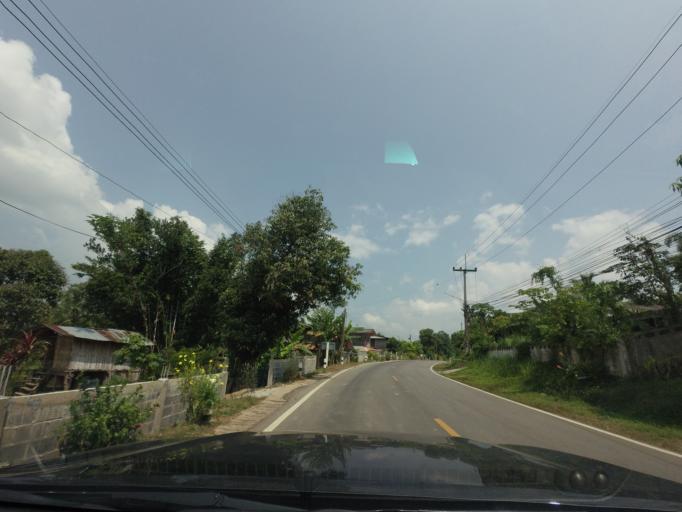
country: TH
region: Nan
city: Santi Suk
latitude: 18.9573
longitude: 100.9236
